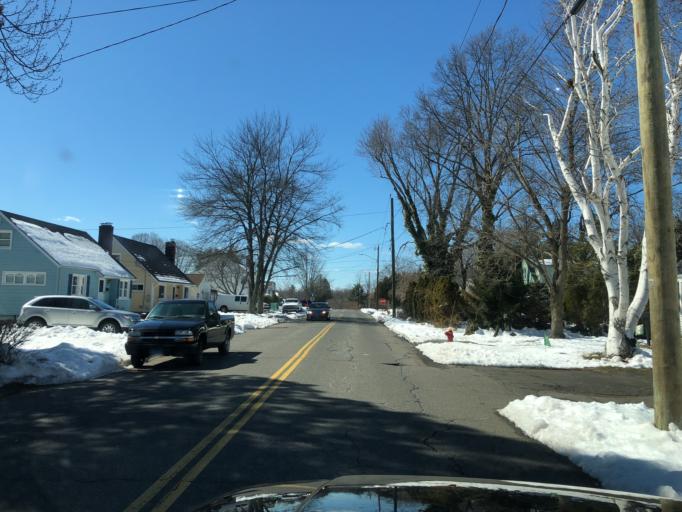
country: US
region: Connecticut
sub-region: Hartford County
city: Newington
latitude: 41.6861
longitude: -72.7108
